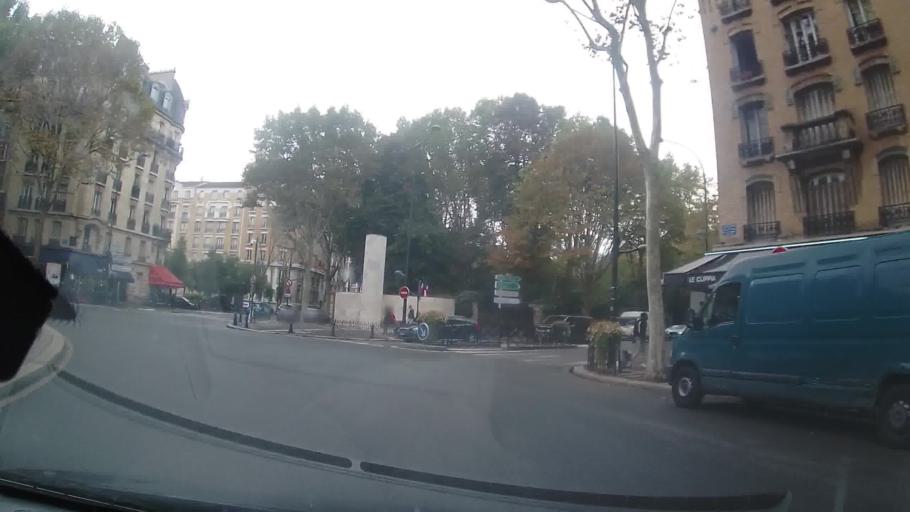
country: FR
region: Ile-de-France
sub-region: Departement des Hauts-de-Seine
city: Clichy
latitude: 48.9033
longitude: 2.3133
